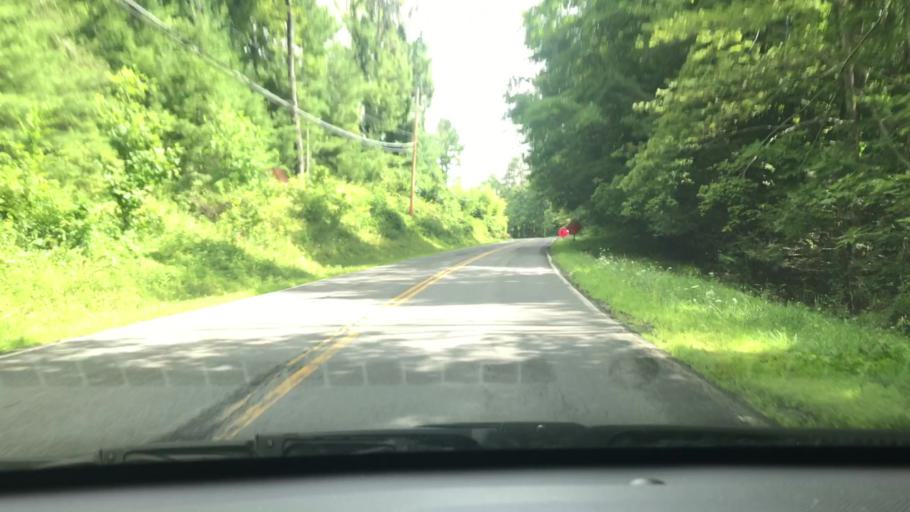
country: US
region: New York
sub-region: Ulster County
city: Shokan
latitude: 41.9821
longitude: -74.2755
